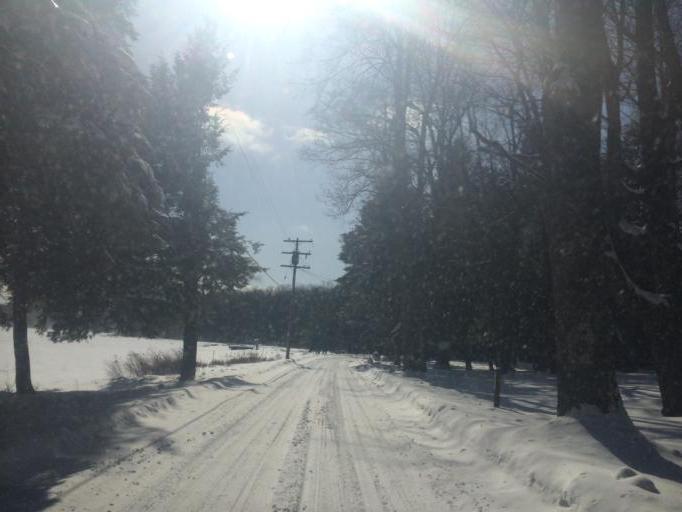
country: US
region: Pennsylvania
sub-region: Centre County
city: Stormstown
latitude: 40.9077
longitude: -78.0580
